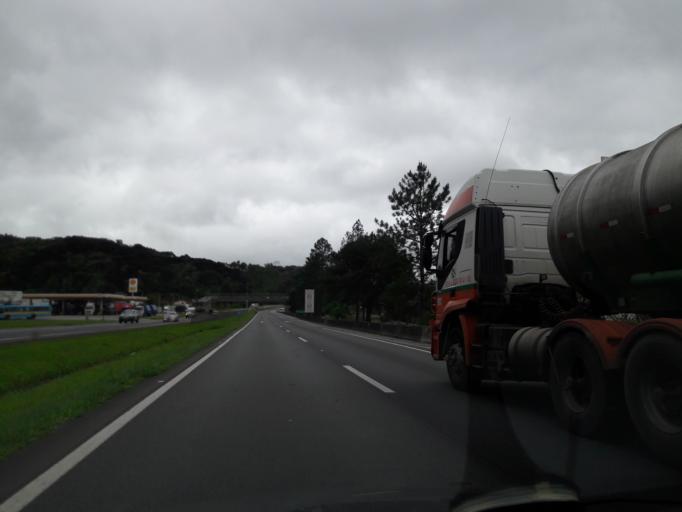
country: BR
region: Parana
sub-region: Campina Grande Do Sul
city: Campina Grande do Sul
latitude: -25.2206
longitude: -48.9050
